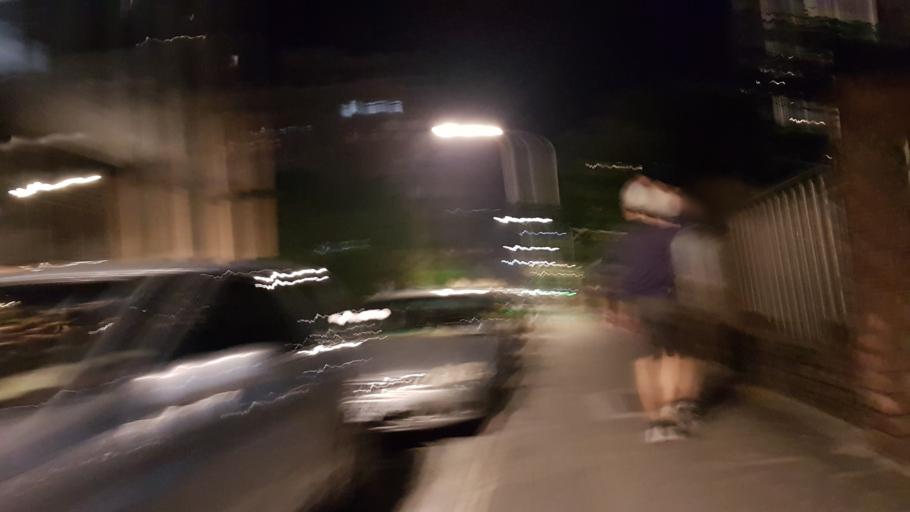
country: TW
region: Taipei
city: Taipei
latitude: 24.9976
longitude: 121.5377
